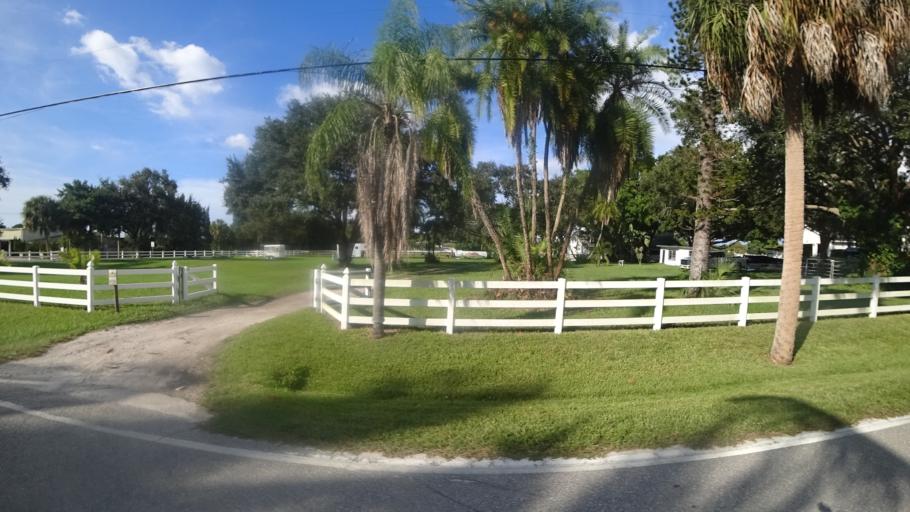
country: US
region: Florida
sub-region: Manatee County
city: West Bradenton
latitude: 27.5262
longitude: -82.6154
